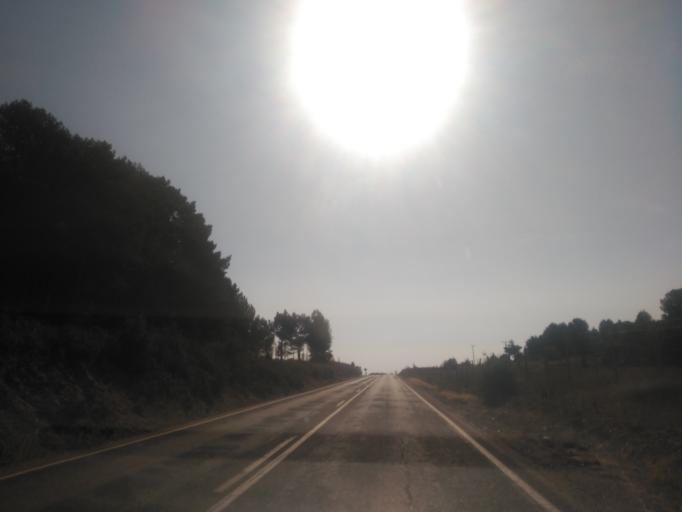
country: ES
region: Castille and Leon
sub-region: Provincia de Soria
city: Casarejos
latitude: 41.8057
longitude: -3.0507
